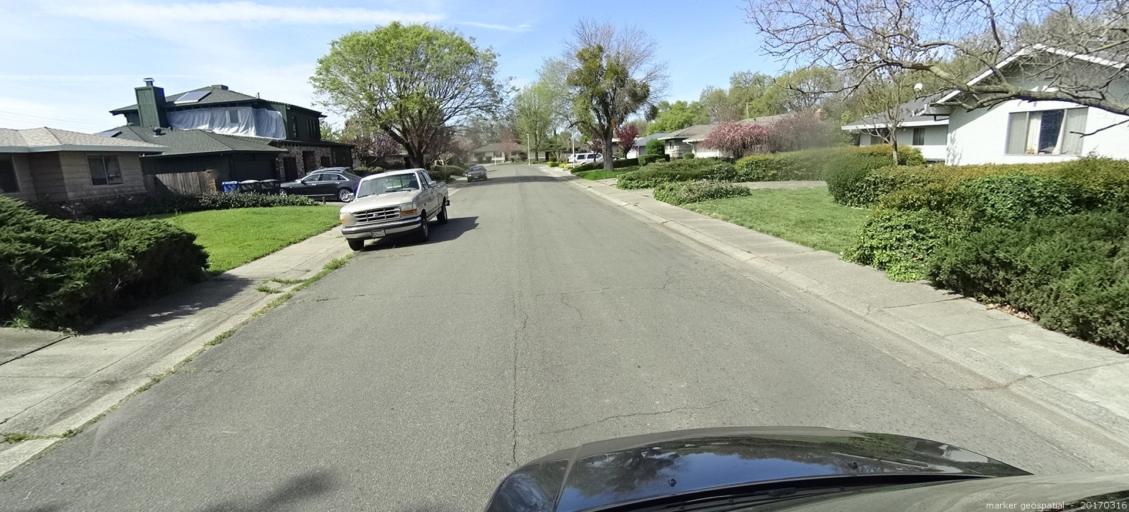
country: US
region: California
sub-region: Sacramento County
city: Parkway
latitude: 38.4972
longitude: -121.4994
